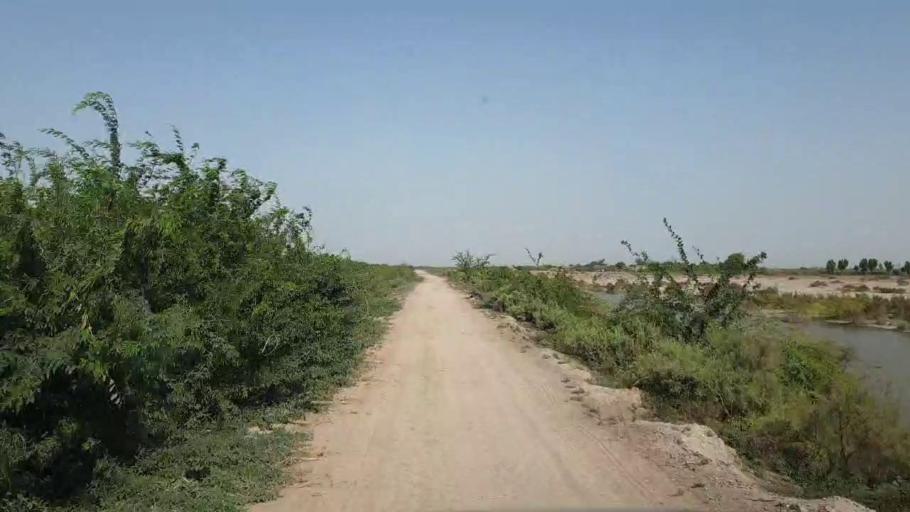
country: PK
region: Sindh
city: Tando Bago
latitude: 24.6462
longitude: 69.0718
